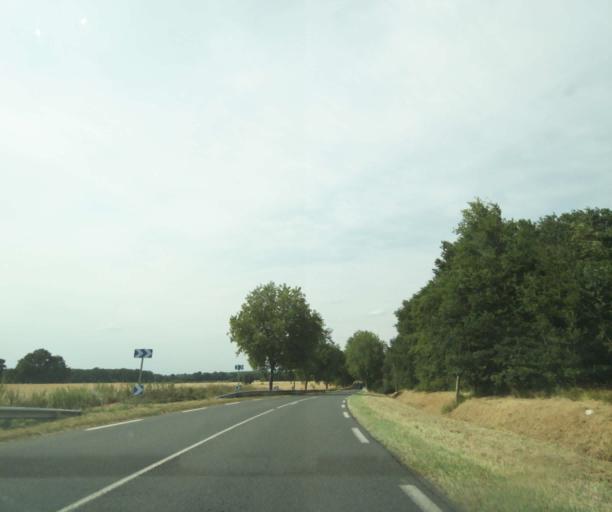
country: FR
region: Centre
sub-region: Departement d'Indre-et-Loire
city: Saint-Paterne-Racan
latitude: 47.6198
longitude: 0.5043
